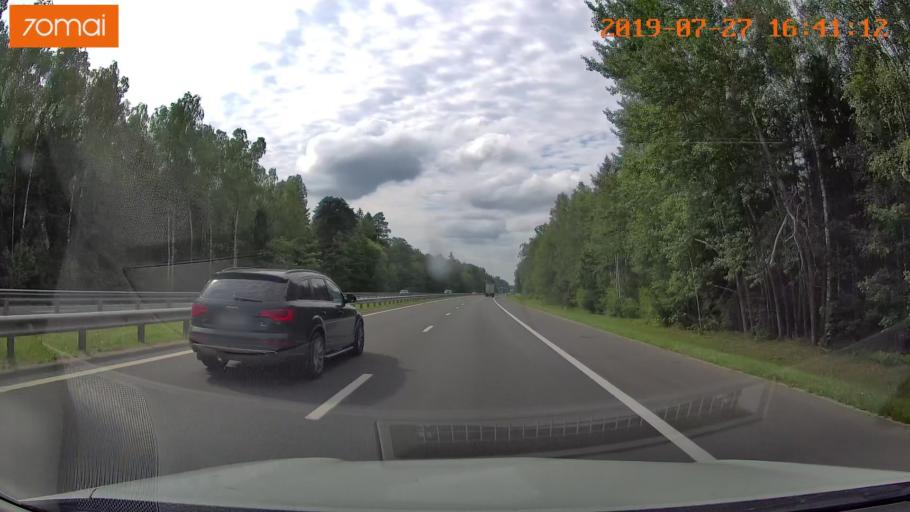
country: RU
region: Kaliningrad
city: Gvardeysk
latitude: 54.6534
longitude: 21.1532
